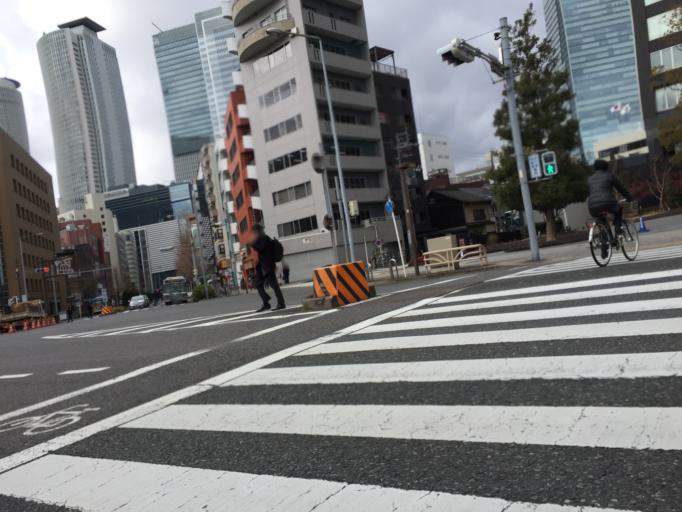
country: JP
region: Aichi
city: Nagoya-shi
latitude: 35.1756
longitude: 136.8860
